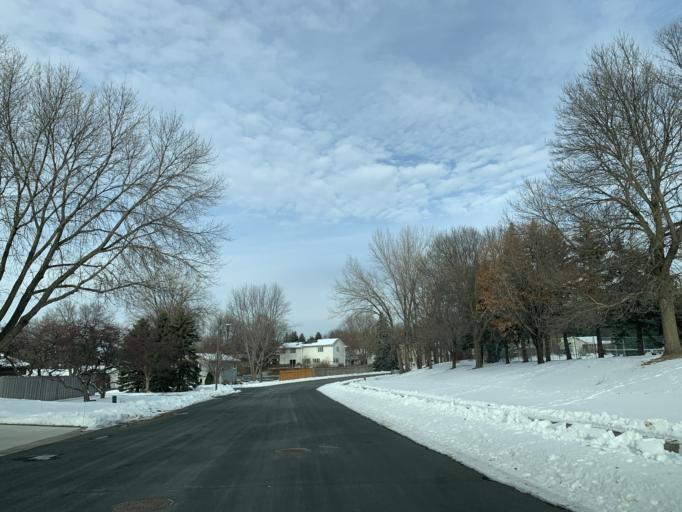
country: US
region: Minnesota
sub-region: Scott County
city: Savage
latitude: 44.8245
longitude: -93.3547
